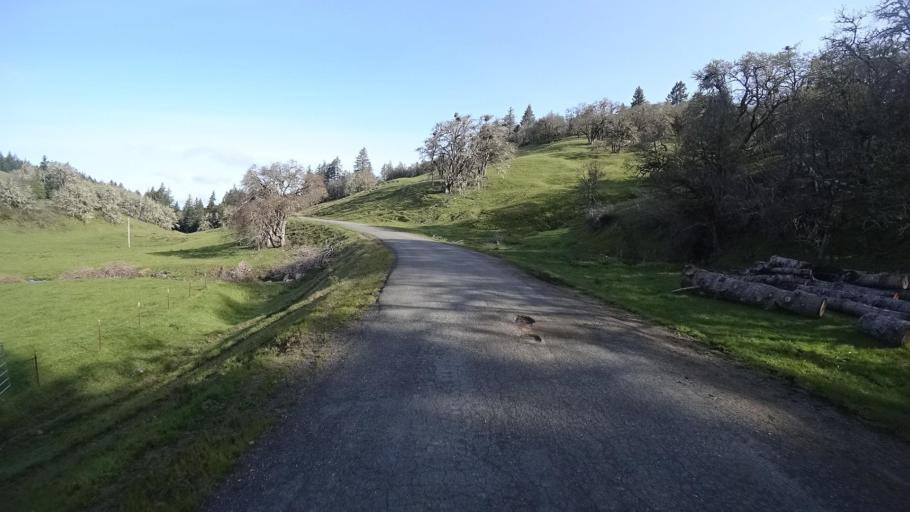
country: US
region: California
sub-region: Humboldt County
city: Hydesville
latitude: 40.6452
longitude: -123.9207
